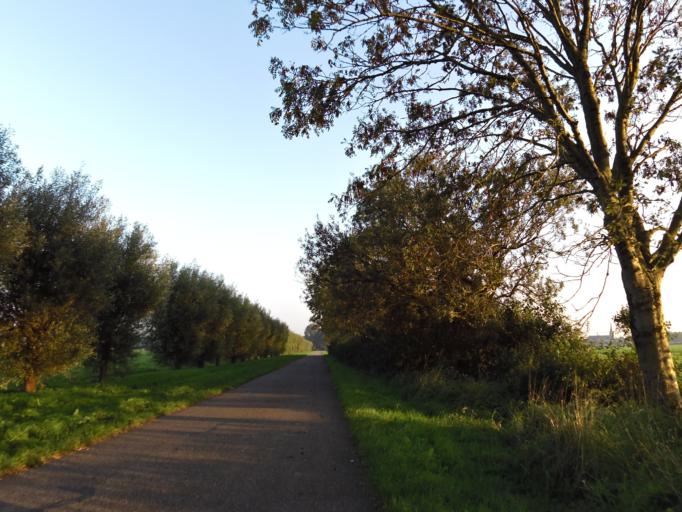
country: NL
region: South Holland
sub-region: Gemeente Leiderdorp
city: Leiderdorp
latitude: 52.1391
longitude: 4.5903
